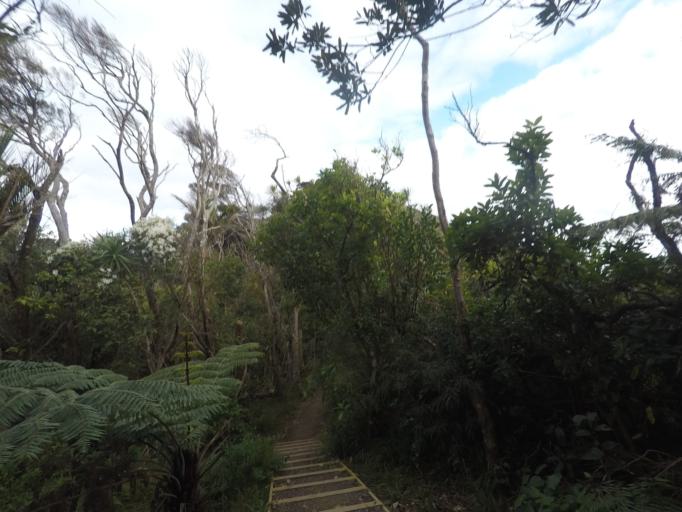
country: NZ
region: Auckland
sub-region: Auckland
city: Muriwai Beach
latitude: -36.9758
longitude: 174.4730
